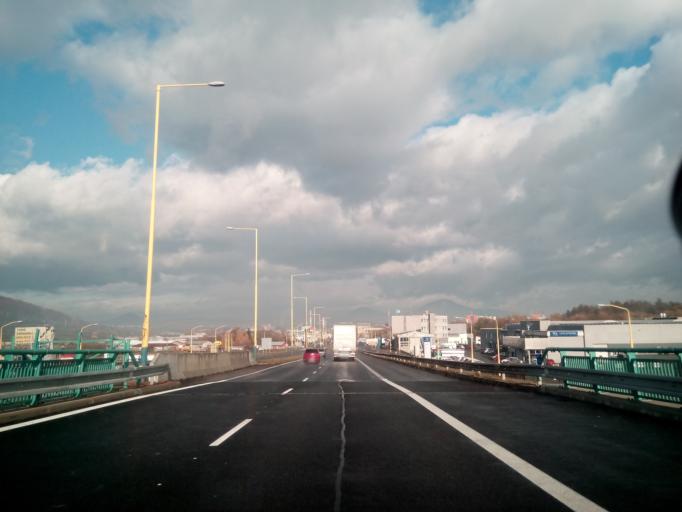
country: SK
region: Presovsky
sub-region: Okres Presov
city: Presov
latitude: 48.9573
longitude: 21.2572
